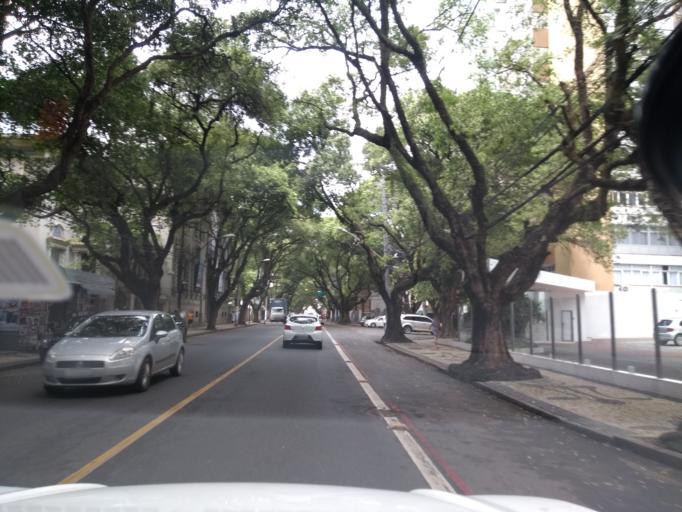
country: BR
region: Bahia
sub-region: Salvador
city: Salvador
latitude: -12.9930
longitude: -38.5260
